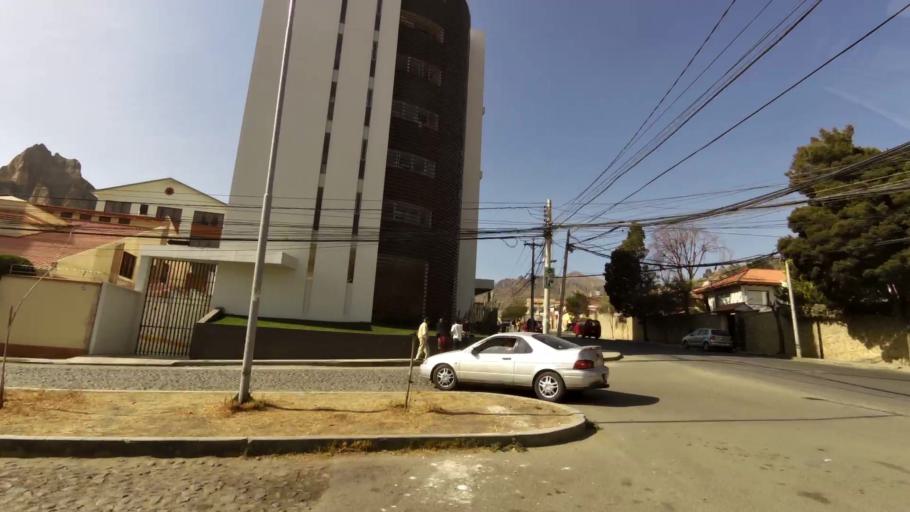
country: BO
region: La Paz
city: La Paz
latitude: -16.5158
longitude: -68.0612
